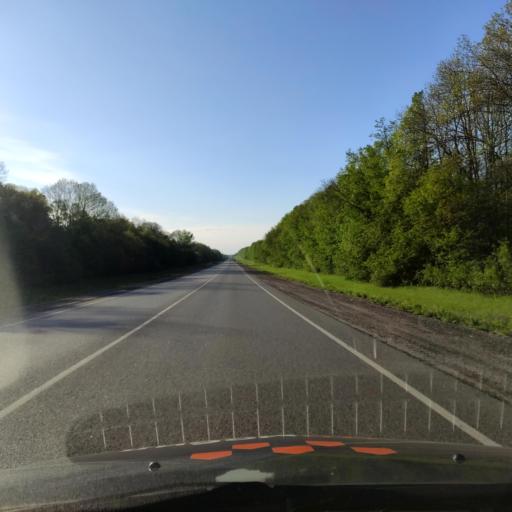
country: RU
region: Lipetsk
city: Yelets
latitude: 52.5741
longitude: 38.6521
